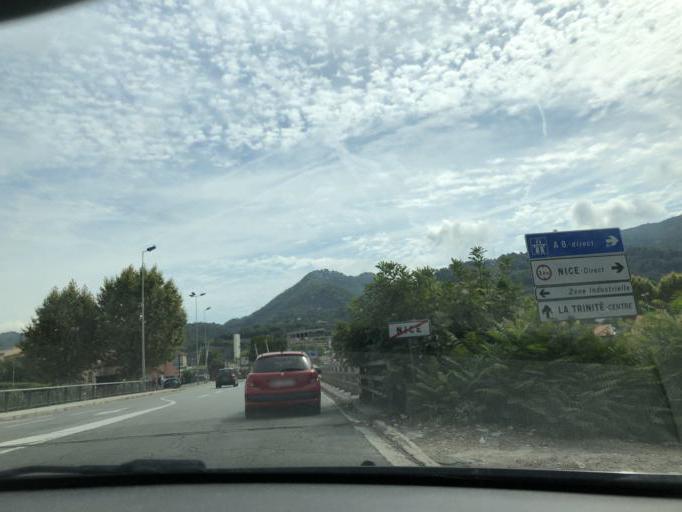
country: FR
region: Provence-Alpes-Cote d'Azur
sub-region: Departement des Alpes-Maritimes
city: La Trinite
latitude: 43.7410
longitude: 7.3092
